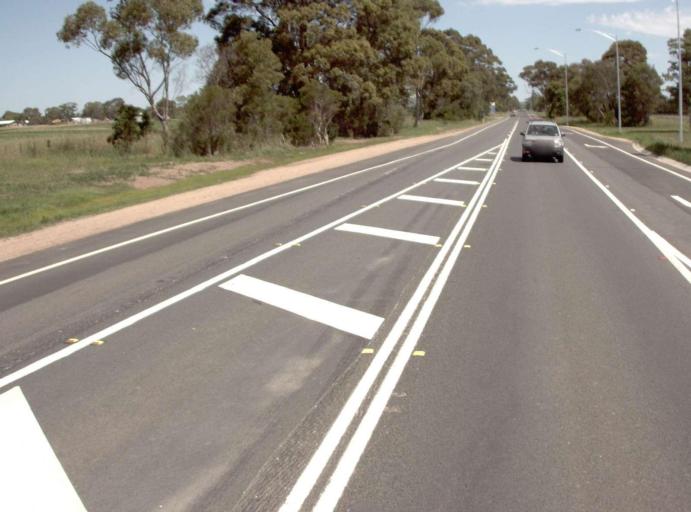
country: AU
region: Victoria
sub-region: Wellington
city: Sale
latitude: -38.0800
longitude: 147.0716
